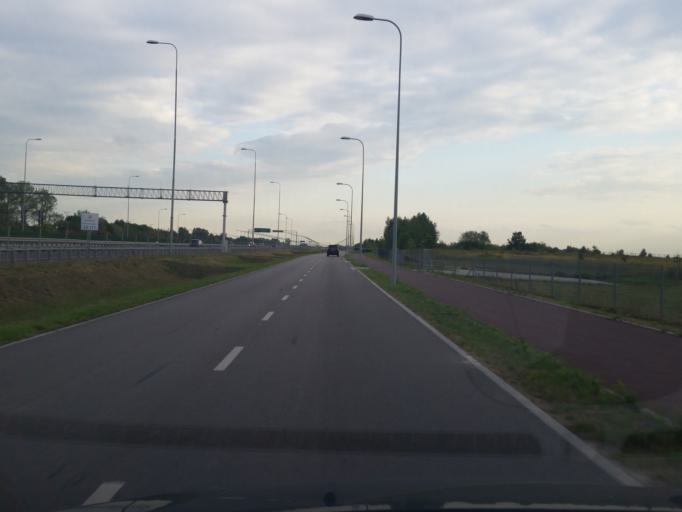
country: PL
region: Masovian Voivodeship
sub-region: Warszawa
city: Wlochy
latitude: 52.1496
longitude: 20.9877
